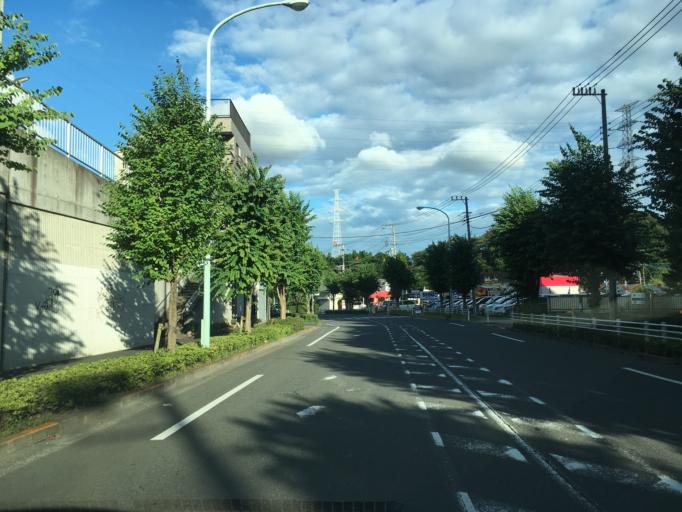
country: JP
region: Tokyo
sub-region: Machida-shi
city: Machida
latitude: 35.5947
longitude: 139.4467
